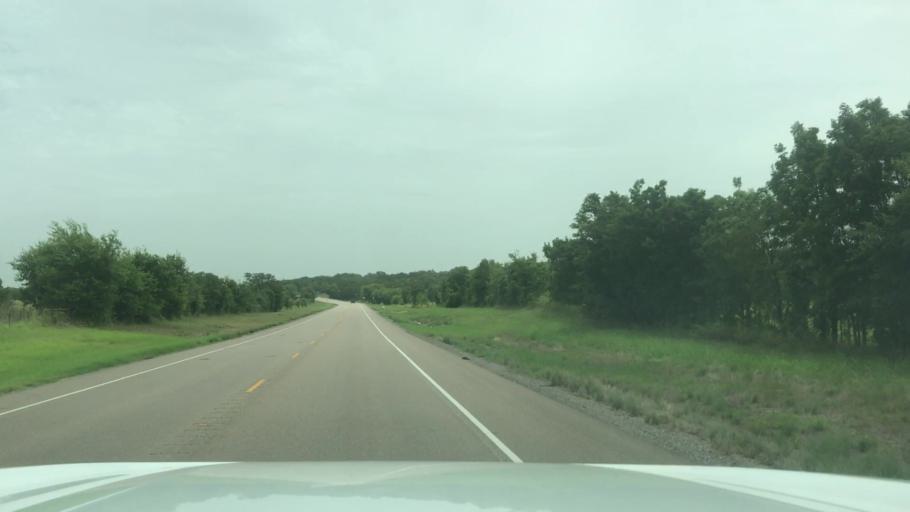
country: US
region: Texas
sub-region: Hamilton County
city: Hico
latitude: 31.9773
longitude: -97.8866
